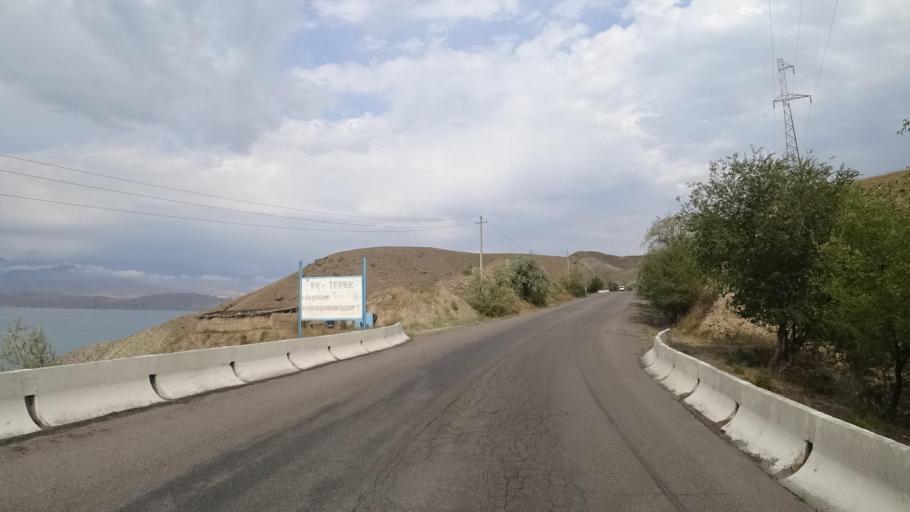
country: KG
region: Jalal-Abad
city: Toktogul
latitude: 41.7789
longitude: 72.9838
